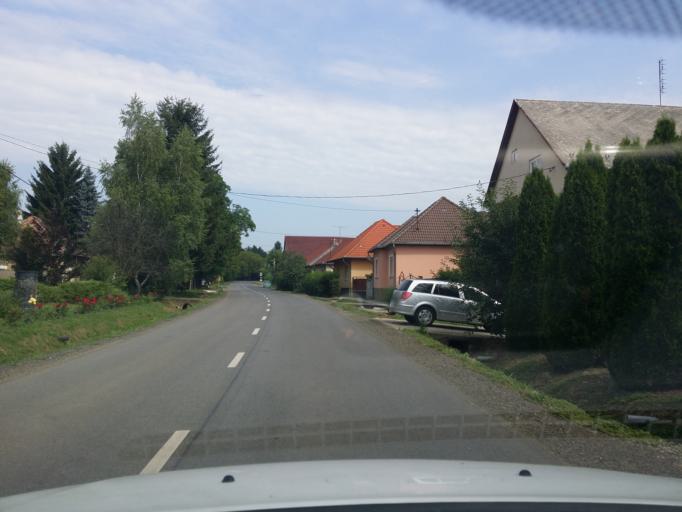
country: HU
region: Pest
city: Acsa
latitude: 47.7790
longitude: 19.3645
